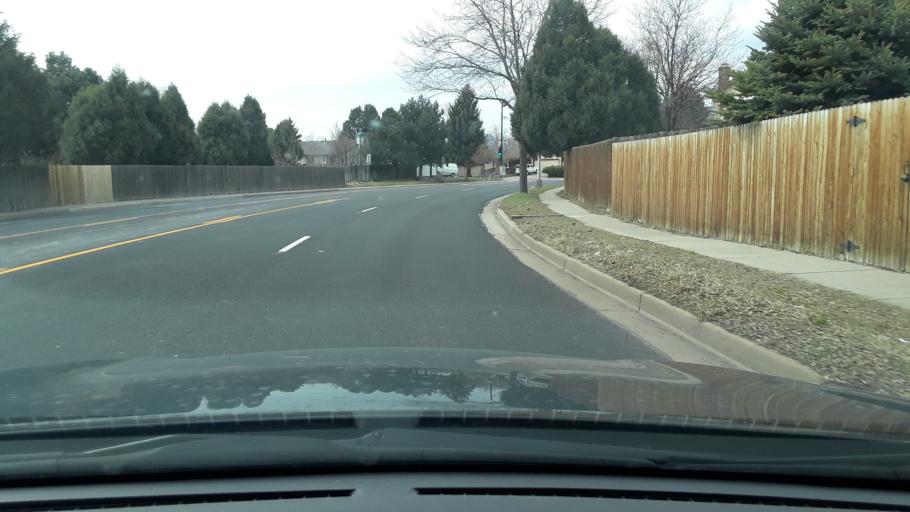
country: US
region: Colorado
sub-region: El Paso County
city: Air Force Academy
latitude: 38.9270
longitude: -104.8374
